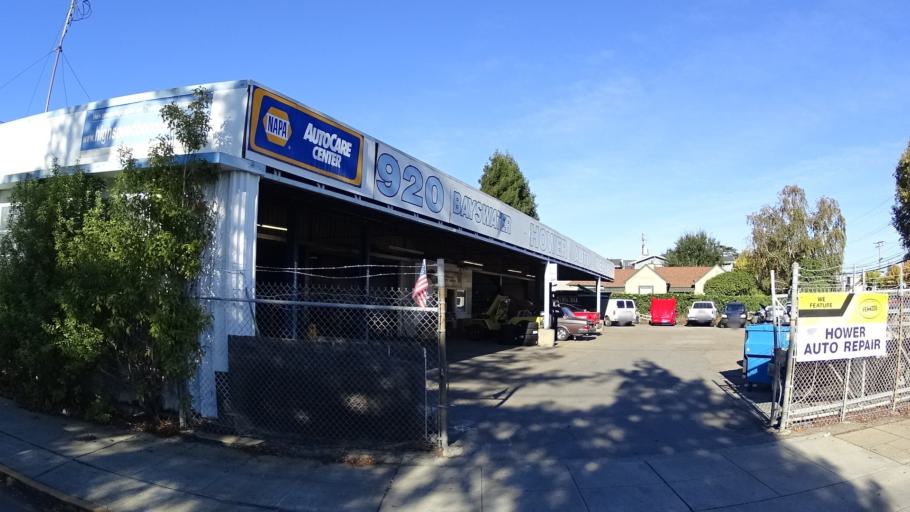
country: US
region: California
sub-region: San Mateo County
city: San Mateo
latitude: 37.5786
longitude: -122.3408
